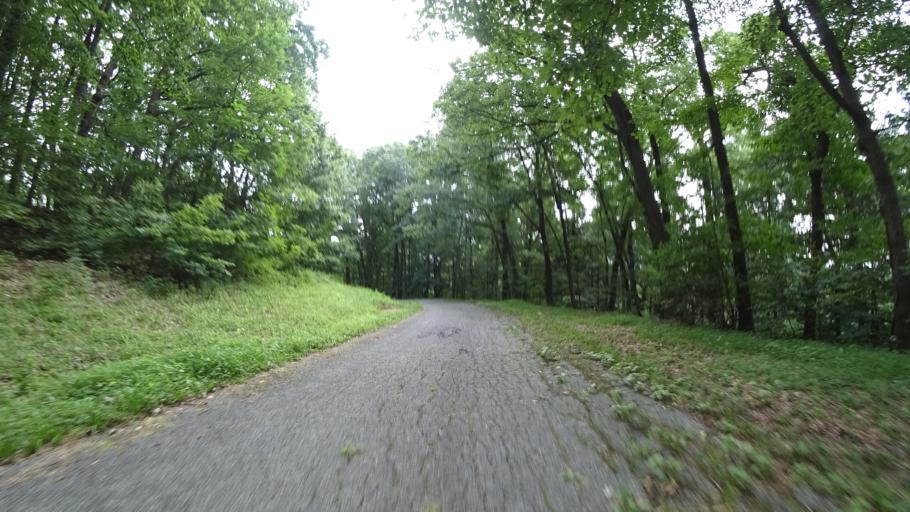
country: US
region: Maryland
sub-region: Prince George's County
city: Mount Rainier
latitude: 38.9097
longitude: -76.9727
